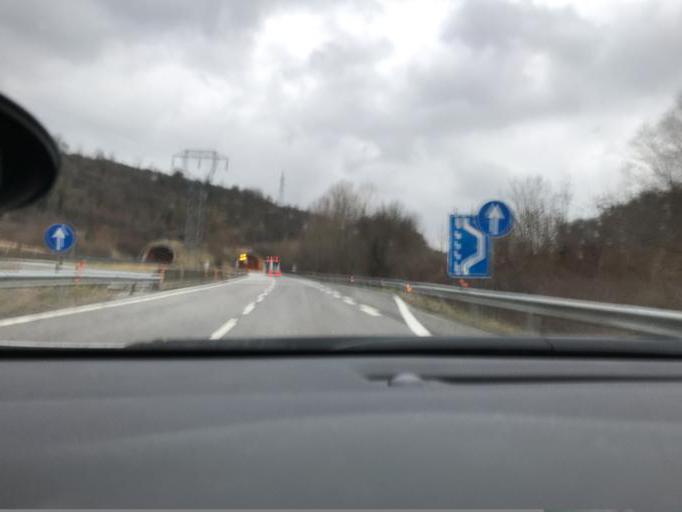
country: IT
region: The Marches
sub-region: Provincia di Ancona
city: Fabriano
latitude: 43.3373
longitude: 12.9346
